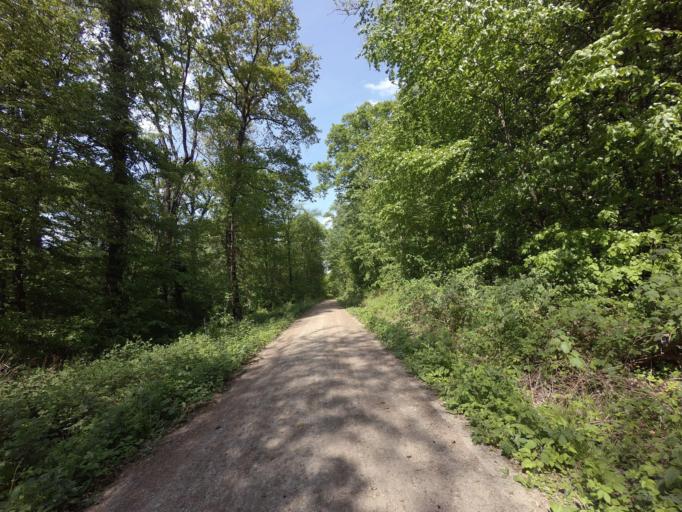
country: DE
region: Lower Saxony
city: Giesen
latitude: 52.1470
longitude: 9.8911
